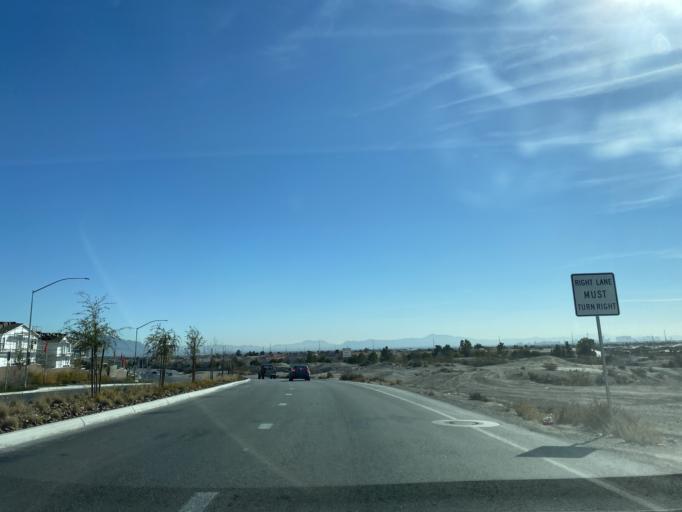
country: US
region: Nevada
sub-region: Clark County
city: North Las Vegas
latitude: 36.2863
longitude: -115.1529
